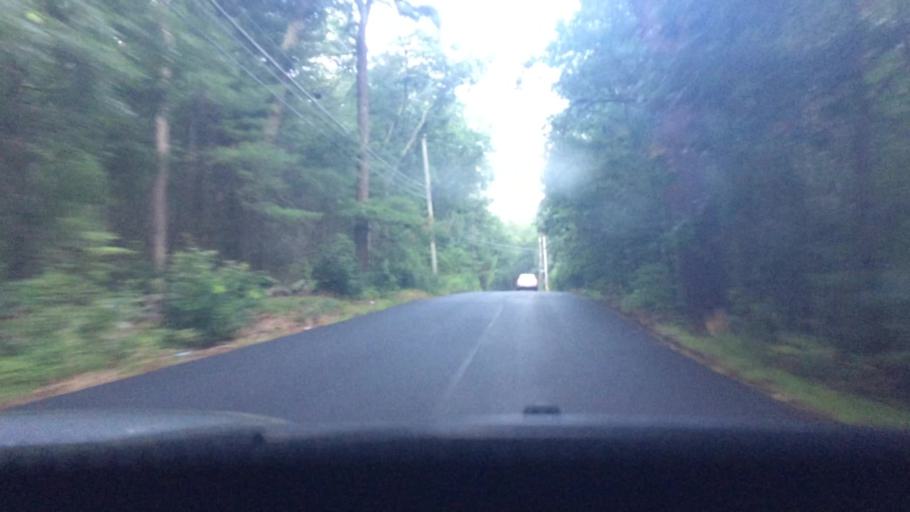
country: US
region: Massachusetts
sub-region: Middlesex County
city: North Reading
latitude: 42.6159
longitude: -71.0928
